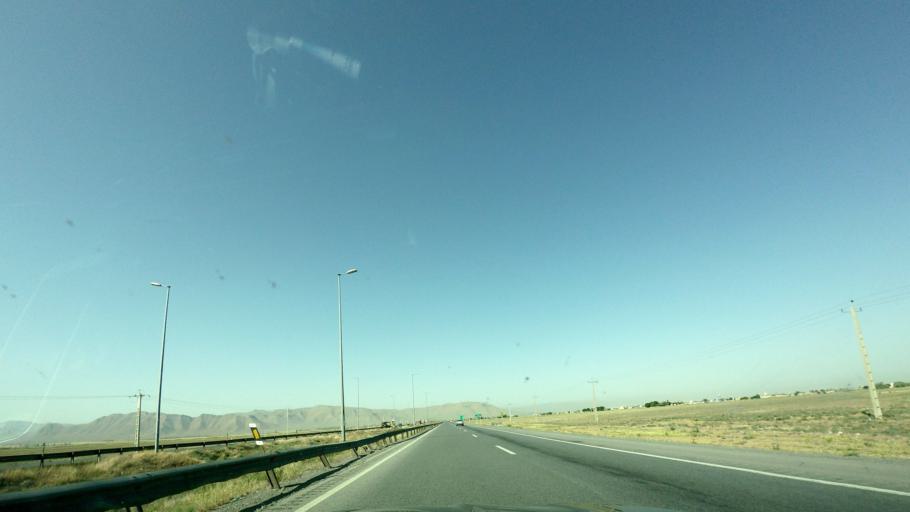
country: IR
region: Markazi
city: Ashtian
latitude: 34.1760
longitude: 50.0402
